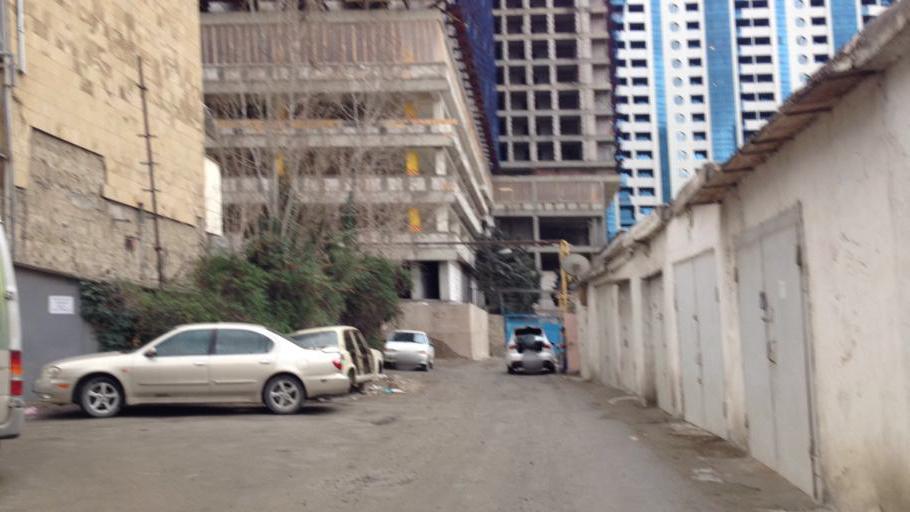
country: AZ
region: Baki
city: Baku
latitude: 40.3803
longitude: 49.8746
